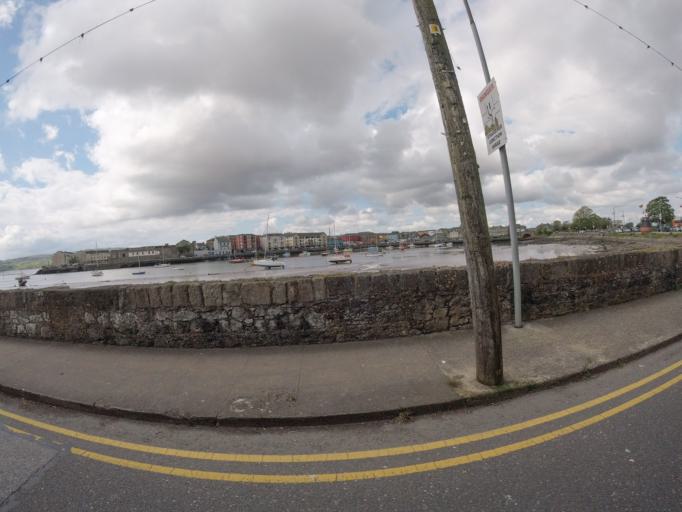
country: IE
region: Munster
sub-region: Waterford
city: Dungarvan
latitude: 52.0915
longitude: -7.6152
